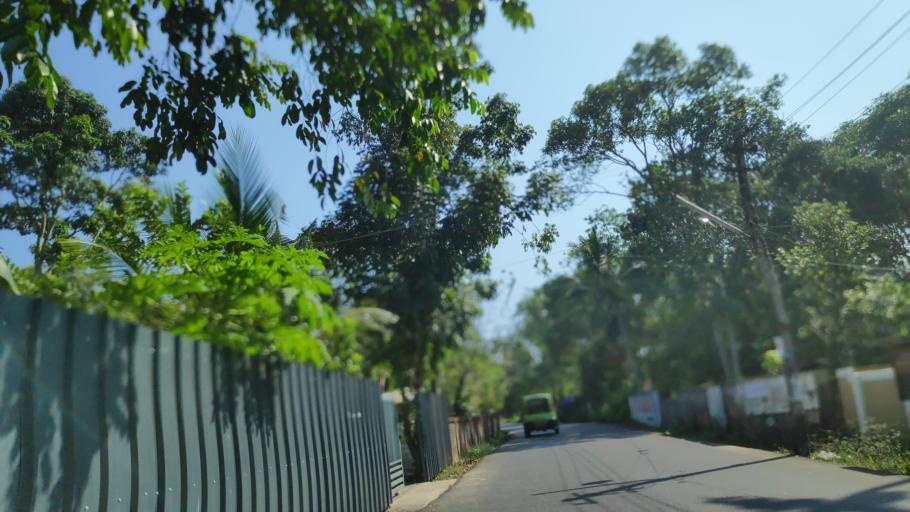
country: IN
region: Kerala
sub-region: Alappuzha
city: Alleppey
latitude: 9.5750
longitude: 76.3164
